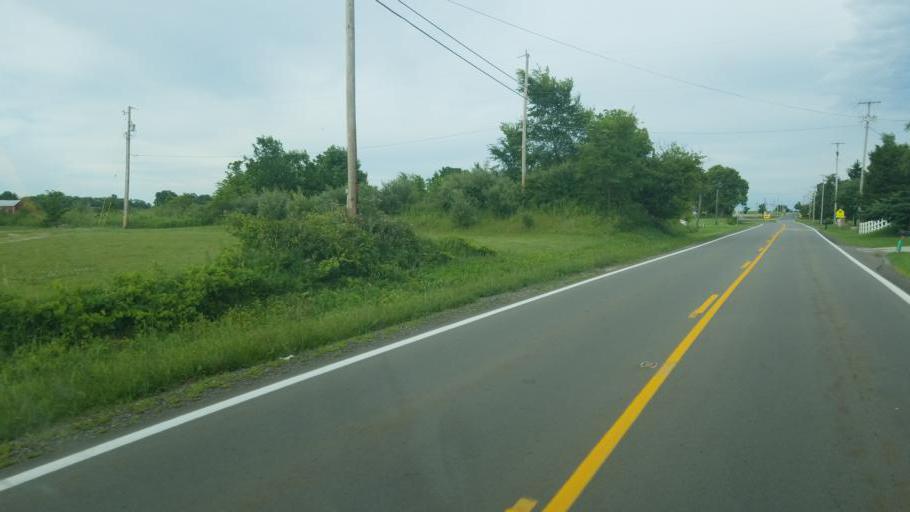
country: US
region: Ohio
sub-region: Morrow County
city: Mount Gilead
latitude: 40.5161
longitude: -82.8402
